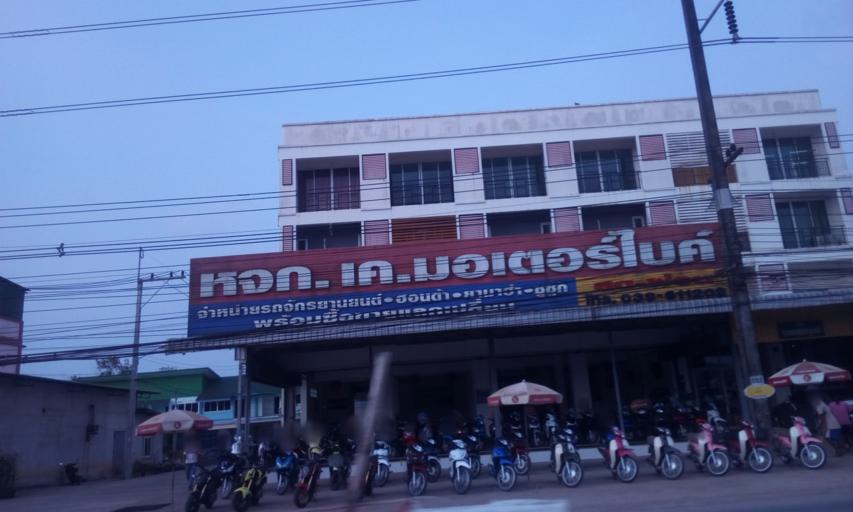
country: TH
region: Trat
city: Khao Saming
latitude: 12.3727
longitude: 102.3865
